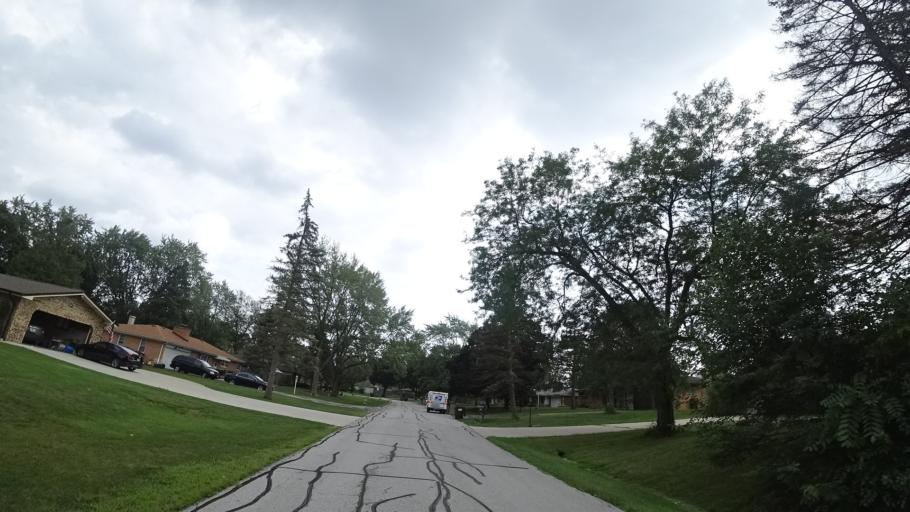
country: US
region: Illinois
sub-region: Cook County
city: Tinley Park
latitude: 41.5946
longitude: -87.7735
